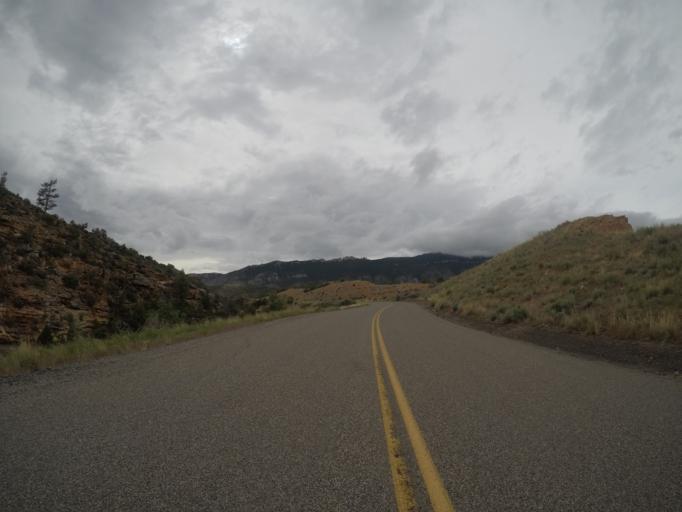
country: US
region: Wyoming
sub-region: Big Horn County
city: Lovell
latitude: 45.1088
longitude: -108.2385
